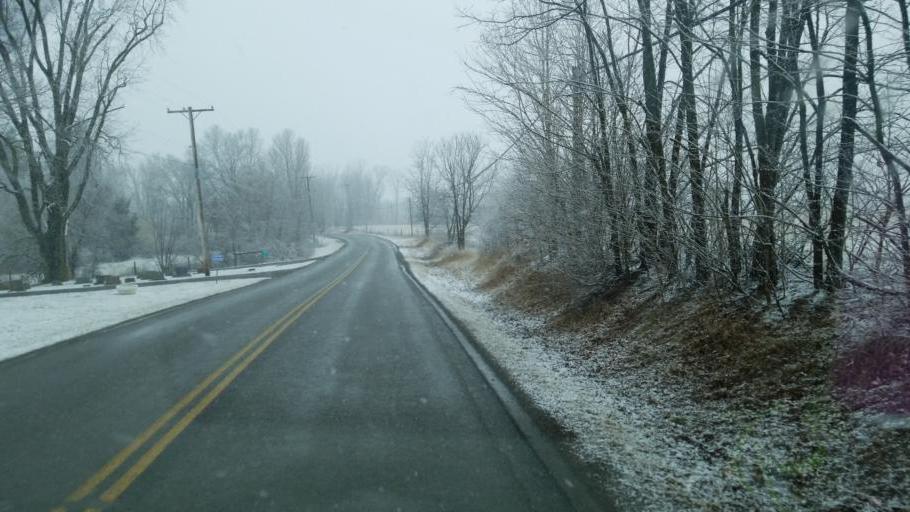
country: US
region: Ohio
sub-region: Logan County
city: Bellefontaine
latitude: 40.3336
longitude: -83.6713
